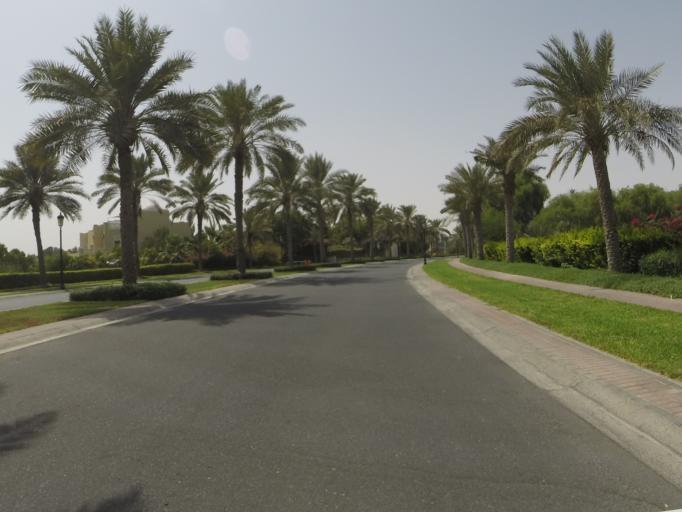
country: AE
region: Dubai
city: Dubai
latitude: 25.0689
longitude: 55.1621
